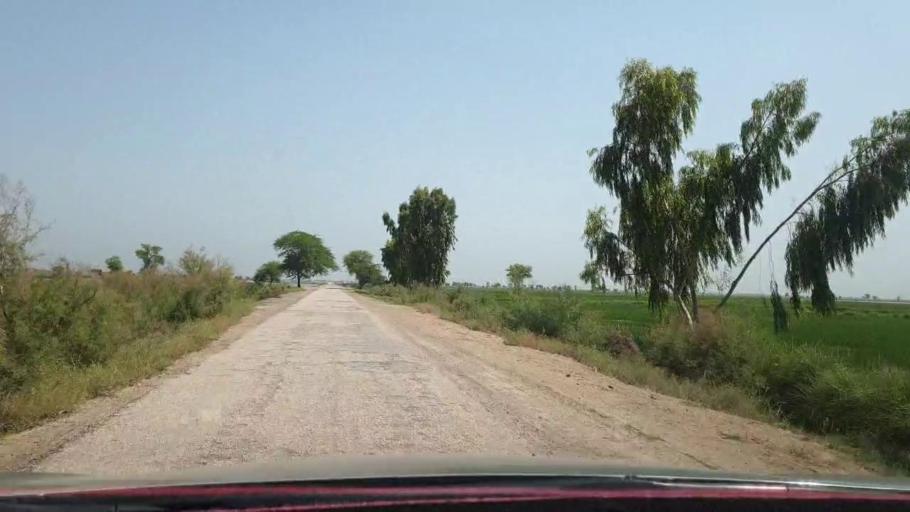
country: PK
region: Sindh
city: Warah
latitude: 27.3810
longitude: 67.7863
